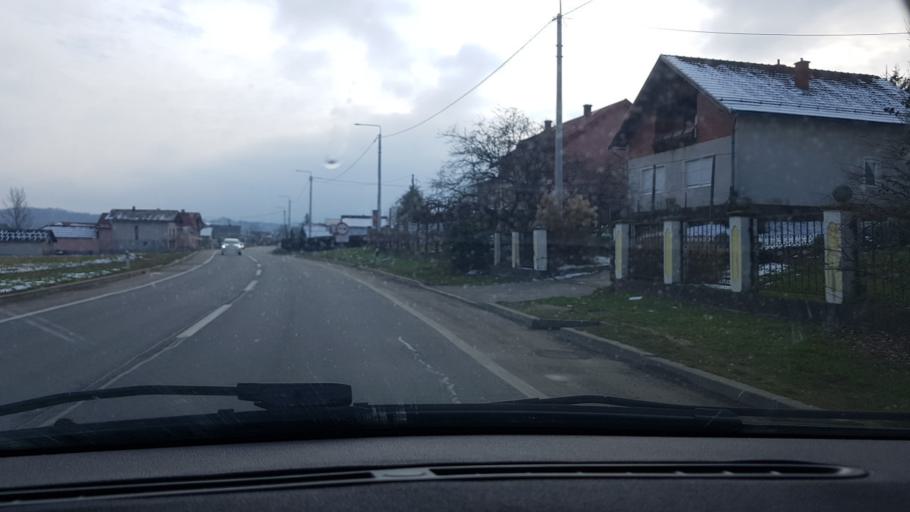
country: HR
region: Varazdinska
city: Tuzno
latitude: 46.2720
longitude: 16.2085
